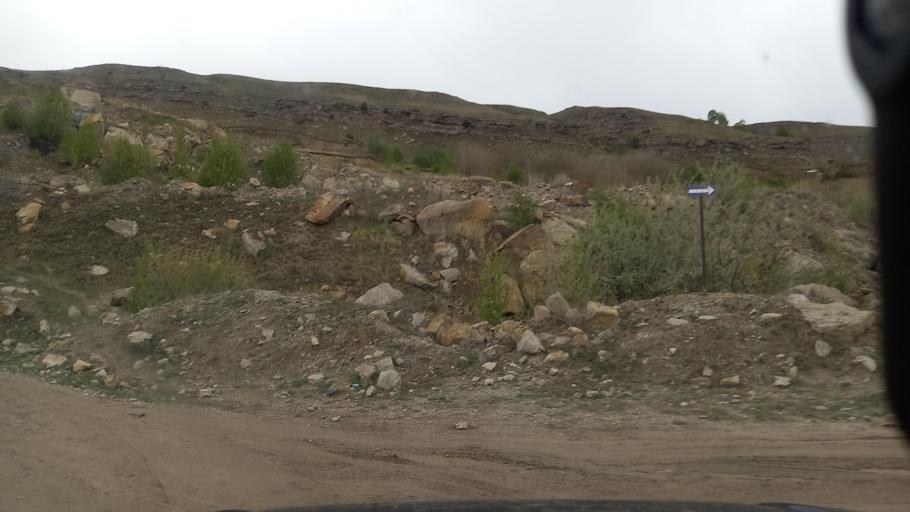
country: RU
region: Kabardino-Balkariya
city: Bylym
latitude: 43.4588
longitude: 42.9951
